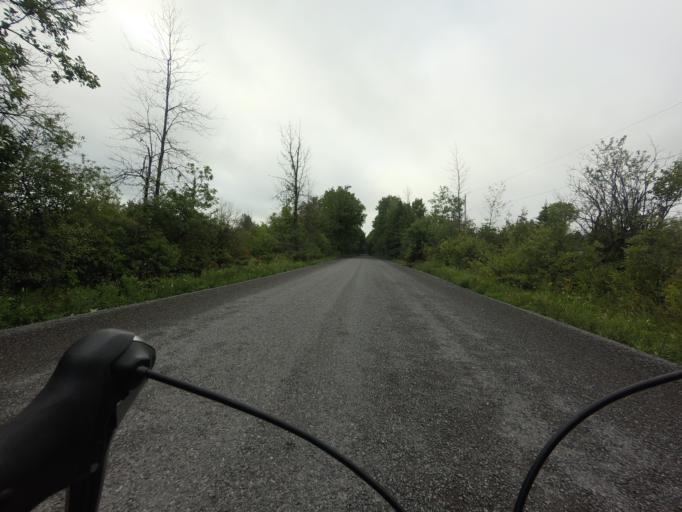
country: CA
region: Ontario
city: Bells Corners
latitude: 45.0745
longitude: -75.7571
